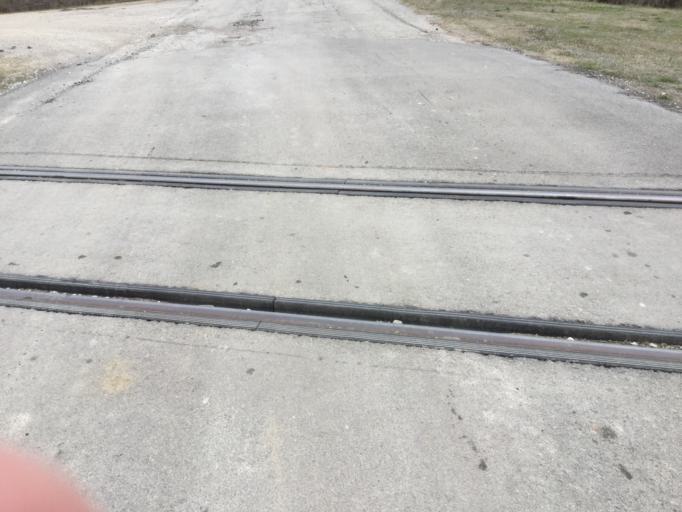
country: US
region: Kansas
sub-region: Wilson County
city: Fredonia
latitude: 37.5398
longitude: -95.8308
